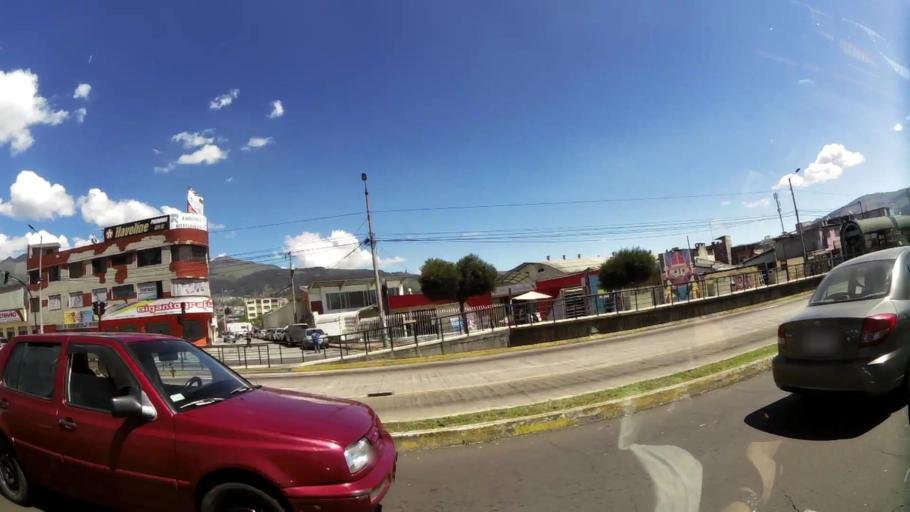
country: EC
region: Pichincha
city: Quito
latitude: -0.1162
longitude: -78.4908
